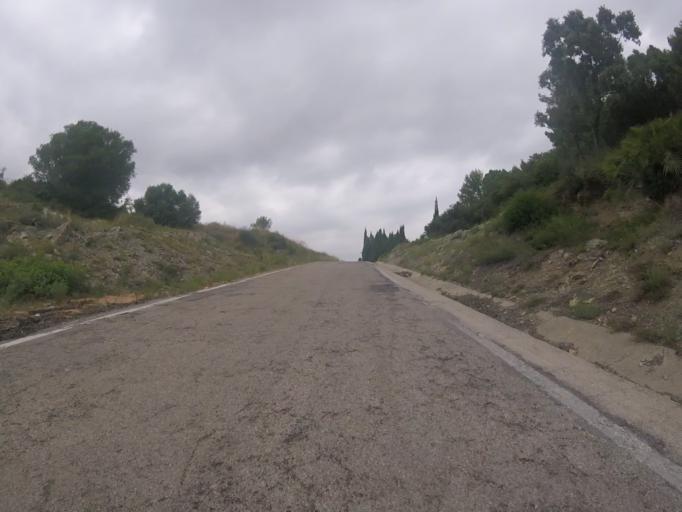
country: ES
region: Valencia
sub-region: Provincia de Castello
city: Cabanes
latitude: 40.1220
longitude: 0.0452
